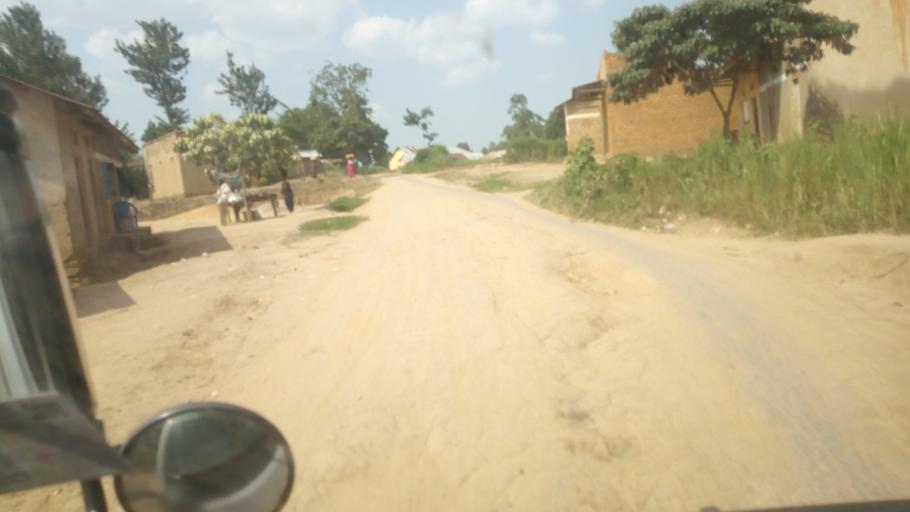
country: UG
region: Western Region
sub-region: Kanungu District
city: Ntungamo
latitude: -0.7895
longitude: 29.6864
